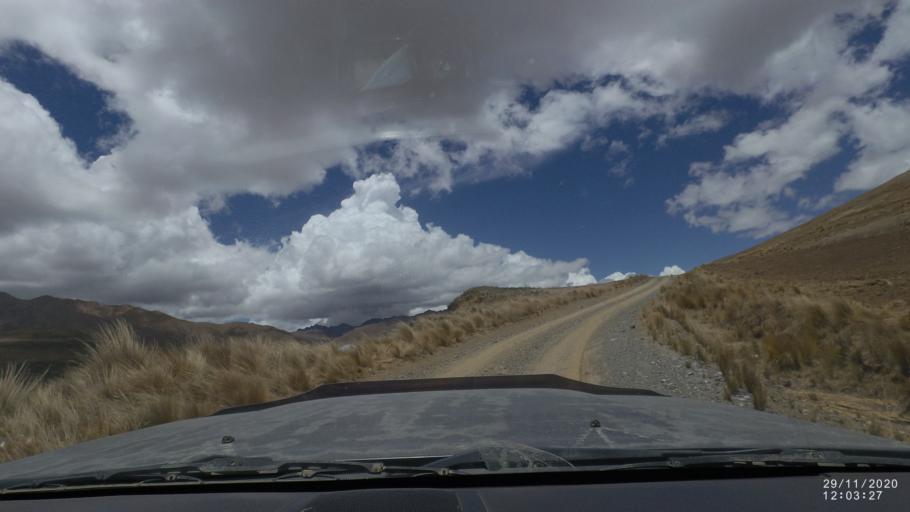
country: BO
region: Cochabamba
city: Cochabamba
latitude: -17.1506
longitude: -66.2857
